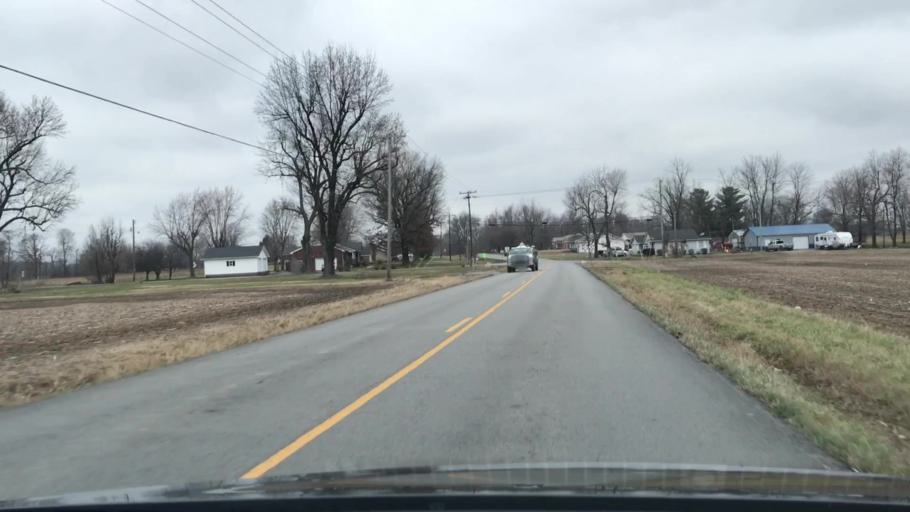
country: US
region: Kentucky
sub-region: Muhlenberg County
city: Morehead
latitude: 37.3556
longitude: -87.2291
